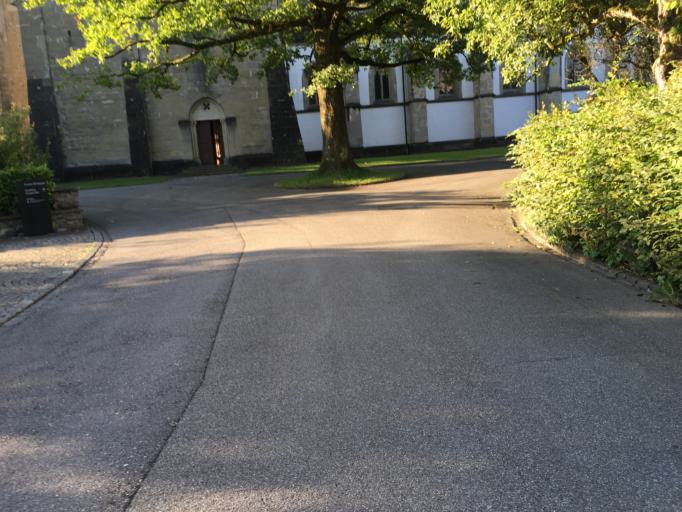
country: CH
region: Zurich
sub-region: Bezirk Affoltern
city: Hausen am Albis / Hausen (Dorf)
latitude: 47.2278
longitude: 8.5245
